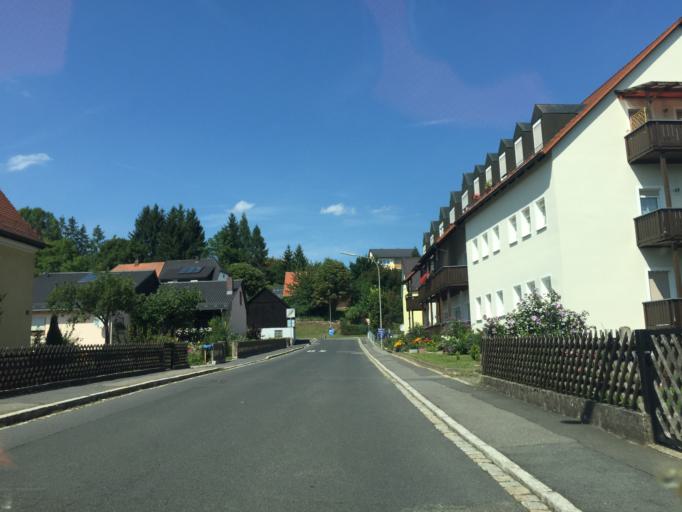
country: DE
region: Bavaria
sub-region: Upper Palatinate
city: Pressath
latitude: 49.7663
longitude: 11.9418
